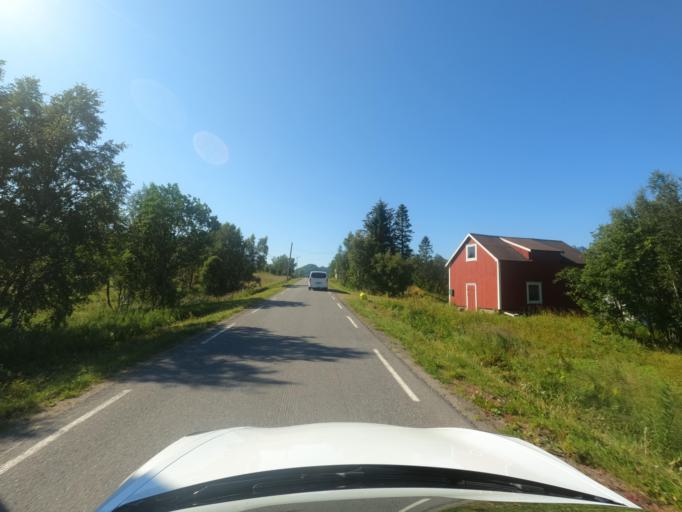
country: NO
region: Nordland
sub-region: Hadsel
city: Stokmarknes
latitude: 68.3171
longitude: 14.9942
